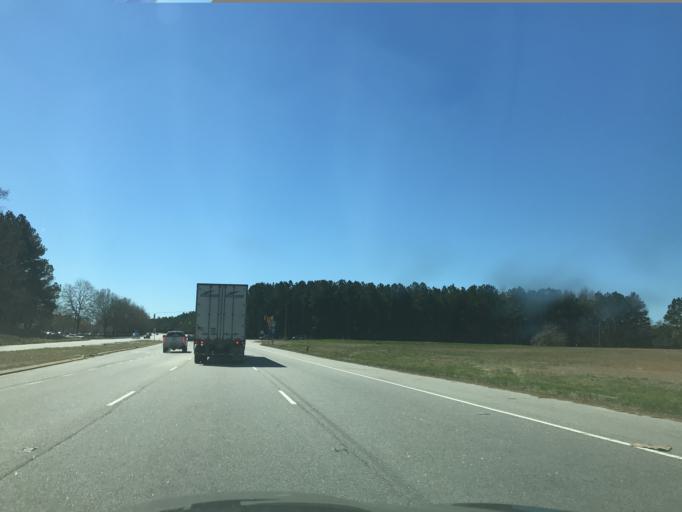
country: US
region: North Carolina
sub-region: Wake County
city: Garner
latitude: 35.7323
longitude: -78.6408
